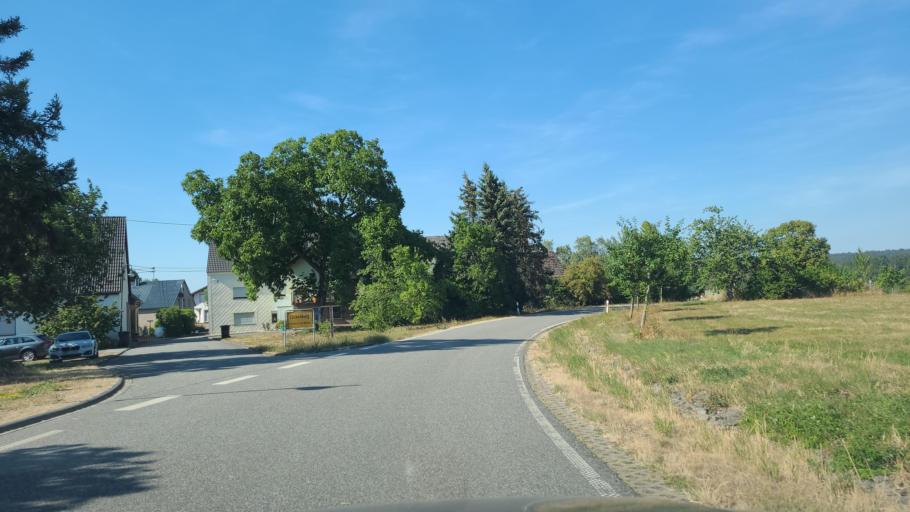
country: DE
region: Rheinland-Pfalz
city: Luckenburg
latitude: 49.7425
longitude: 6.9669
